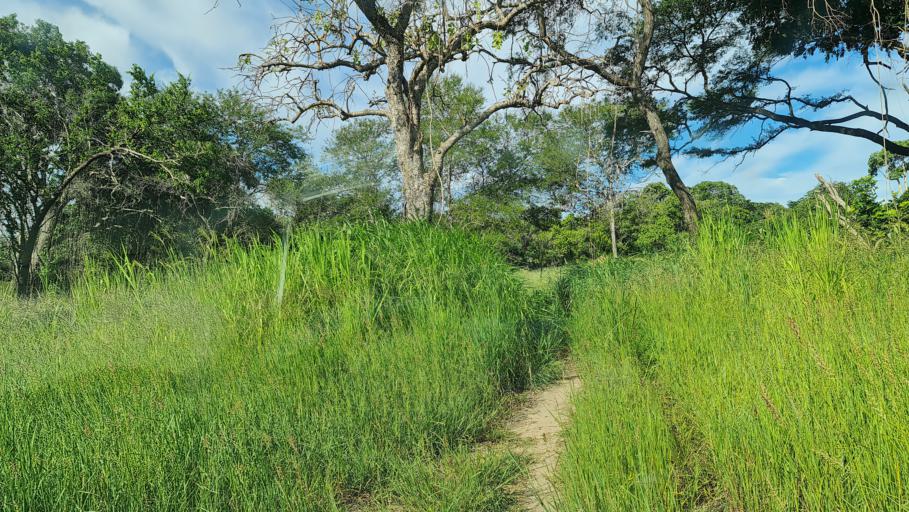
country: MZ
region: Nampula
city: Ilha de Mocambique
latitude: -15.5037
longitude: 40.1567
